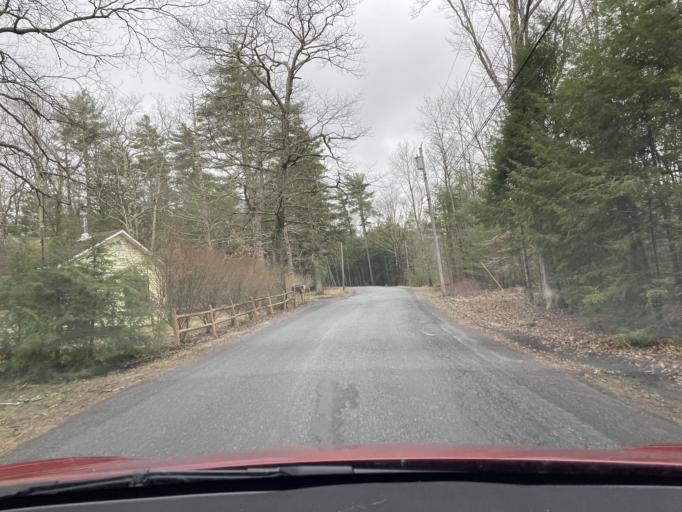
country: US
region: New York
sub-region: Ulster County
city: Manorville
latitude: 42.0955
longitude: -74.0351
